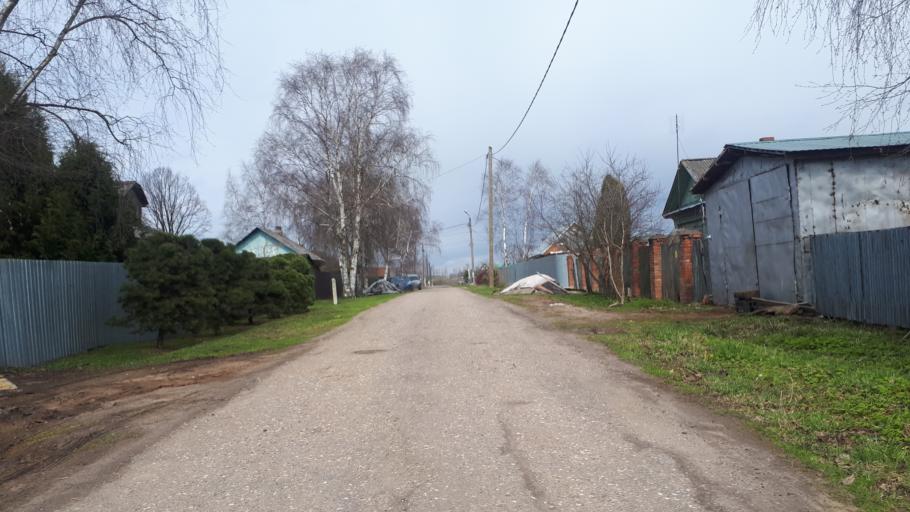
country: RU
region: Jaroslavl
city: Konstantinovskiy
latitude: 57.8283
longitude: 39.5787
